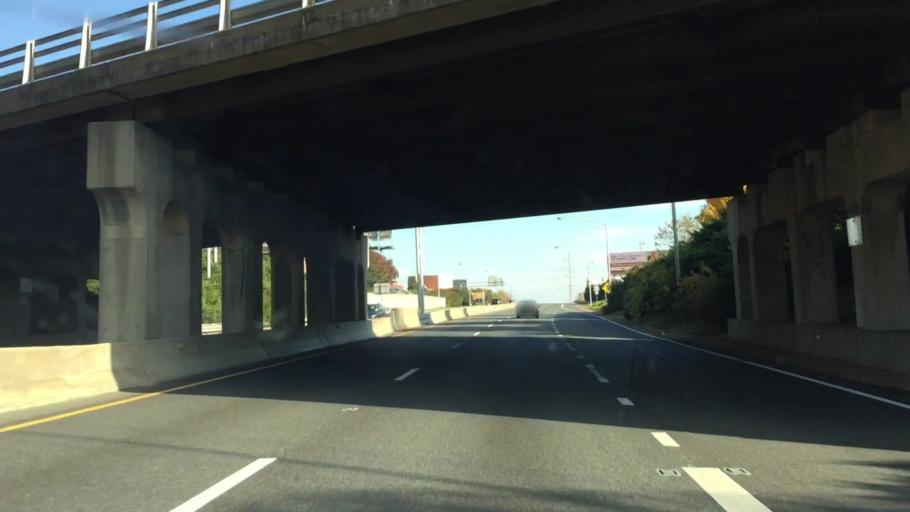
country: US
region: North Carolina
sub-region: Forsyth County
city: Winston-Salem
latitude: 36.0940
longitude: -80.2792
